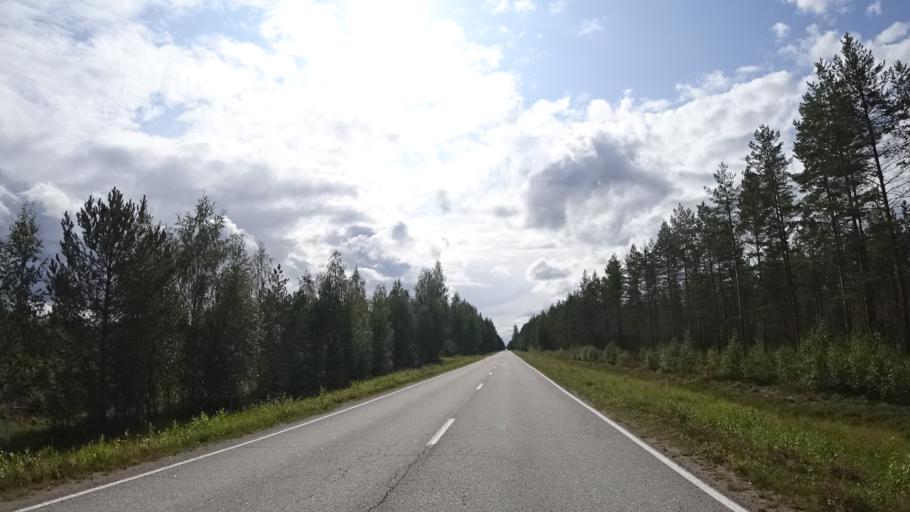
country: FI
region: North Karelia
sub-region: Joensuu
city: Ilomantsi
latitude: 62.7636
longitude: 31.0251
